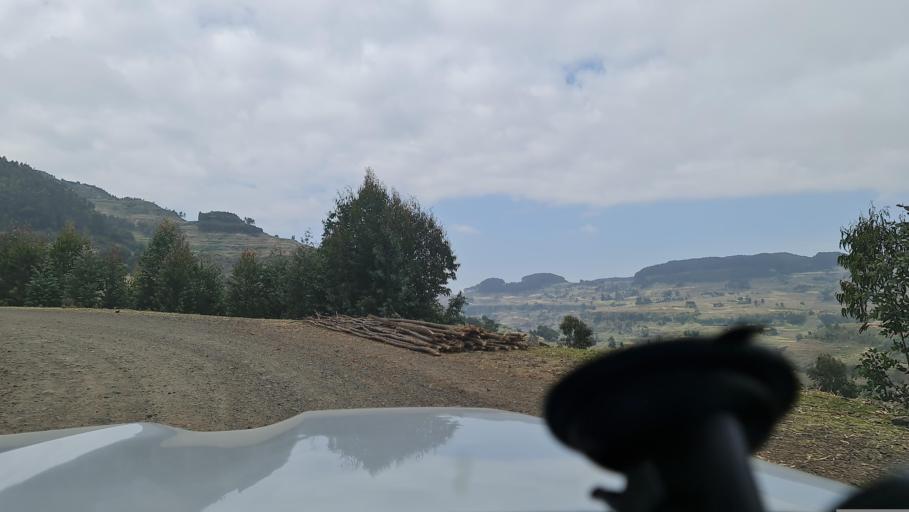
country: ET
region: Amhara
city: Abomsa
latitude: 10.1378
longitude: 39.7894
